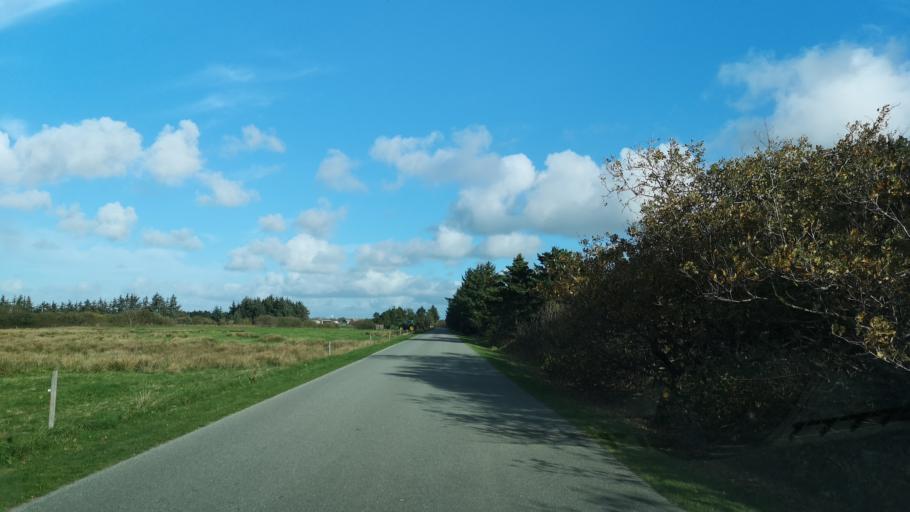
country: DK
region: South Denmark
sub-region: Varde Kommune
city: Oksbol
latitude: 55.7119
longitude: 8.2779
